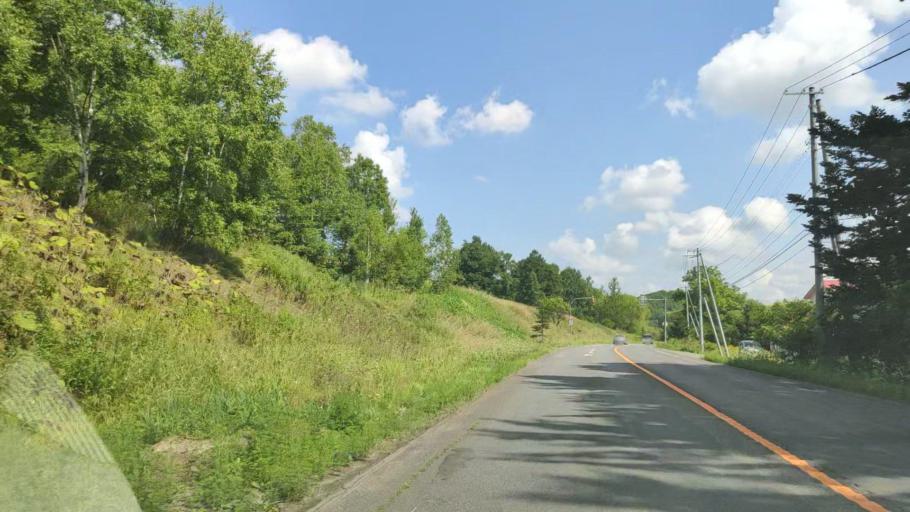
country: JP
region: Hokkaido
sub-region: Asahikawa-shi
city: Asahikawa
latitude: 43.5714
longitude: 142.4375
